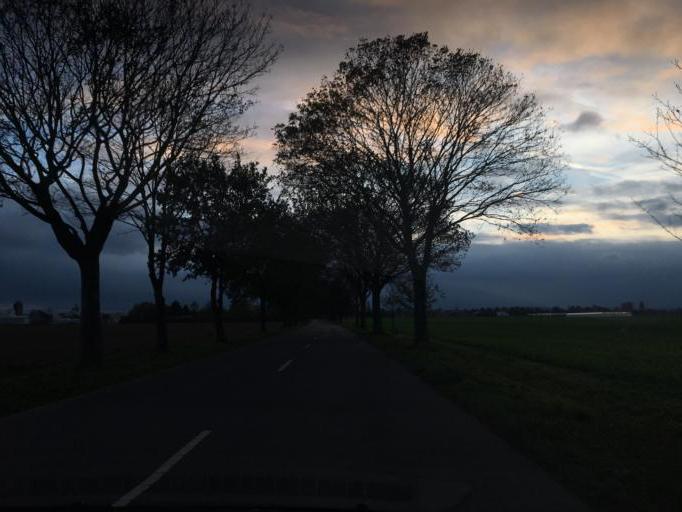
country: DE
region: North Rhine-Westphalia
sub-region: Regierungsbezirk Koln
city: Vettweiss
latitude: 50.7499
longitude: 6.6116
